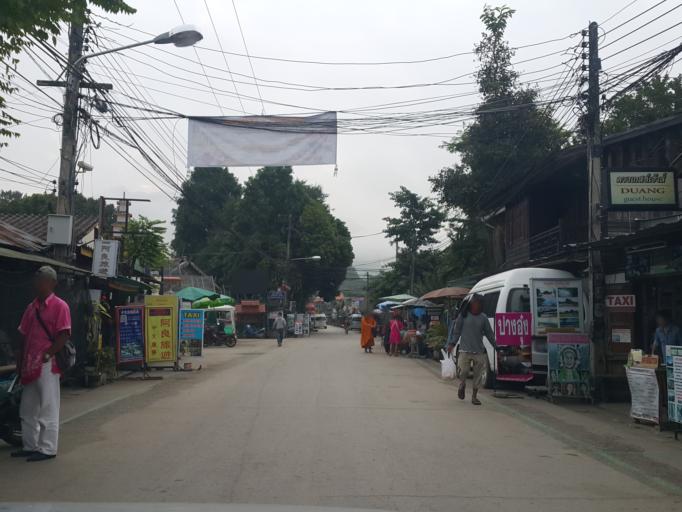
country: TH
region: Chiang Mai
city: Pai
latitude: 19.3599
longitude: 98.4418
